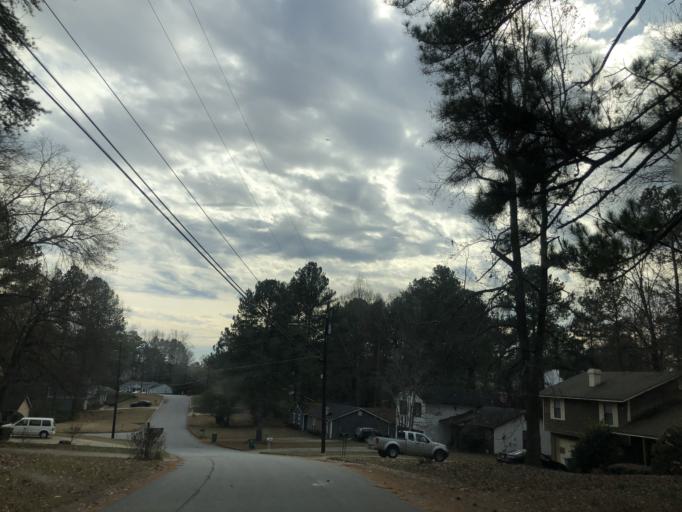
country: US
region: Georgia
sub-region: DeKalb County
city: Panthersville
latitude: 33.6724
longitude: -84.2144
